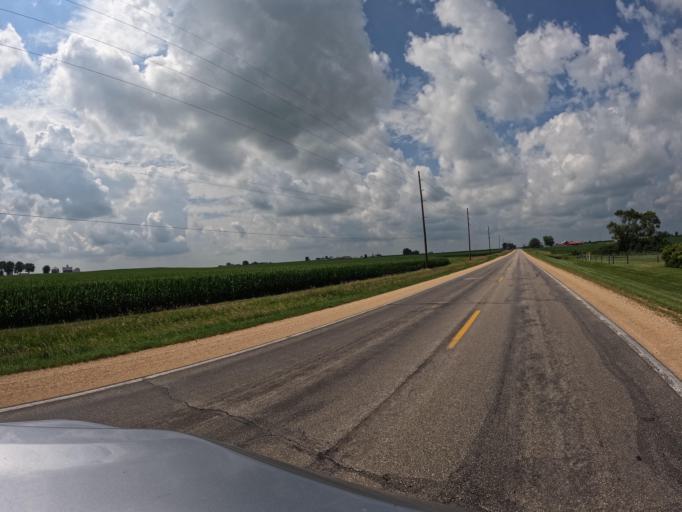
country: US
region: Iowa
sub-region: Clinton County
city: Camanche
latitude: 41.7727
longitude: -90.3547
